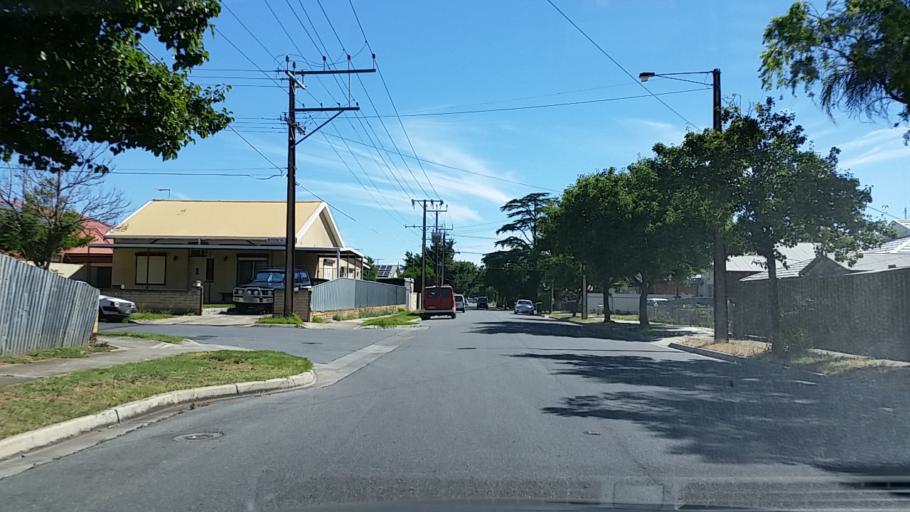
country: AU
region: South Australia
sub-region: Charles Sturt
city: Allenby Gardens
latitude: -34.8895
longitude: 138.5616
